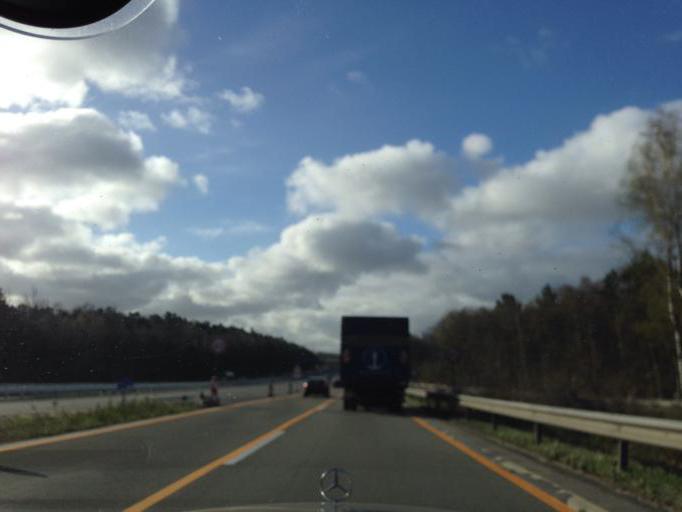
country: DE
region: Lower Saxony
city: Harmstorf
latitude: 53.3786
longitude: 10.0178
